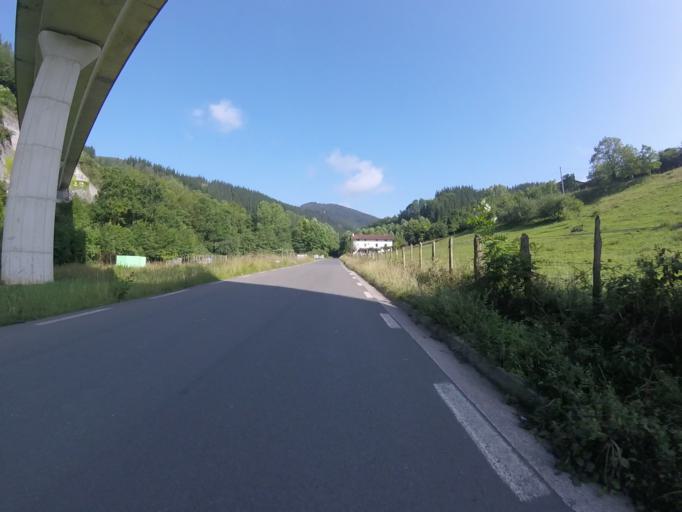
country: ES
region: Basque Country
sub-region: Provincia de Guipuzcoa
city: Ormaiztegui
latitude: 43.0541
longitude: -2.2345
